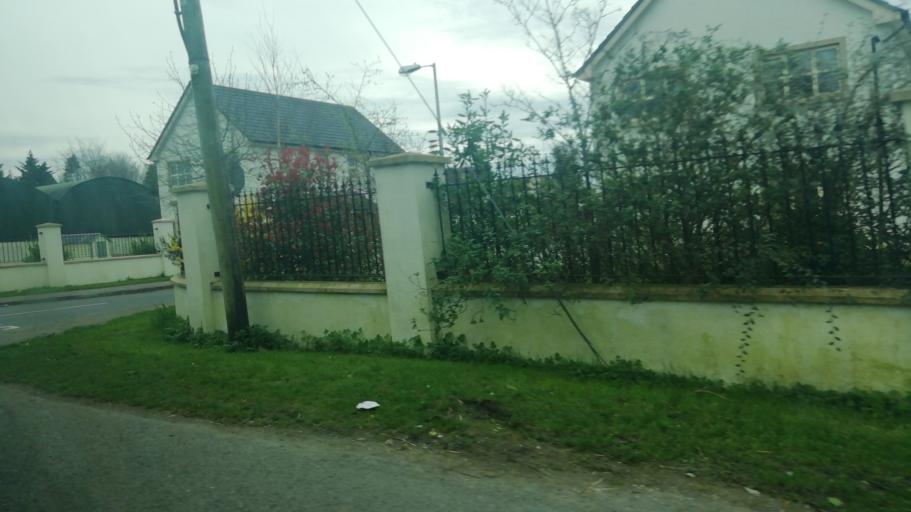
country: IE
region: Leinster
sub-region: Kildare
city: Derrinturn
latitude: 53.3407
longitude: -6.9423
